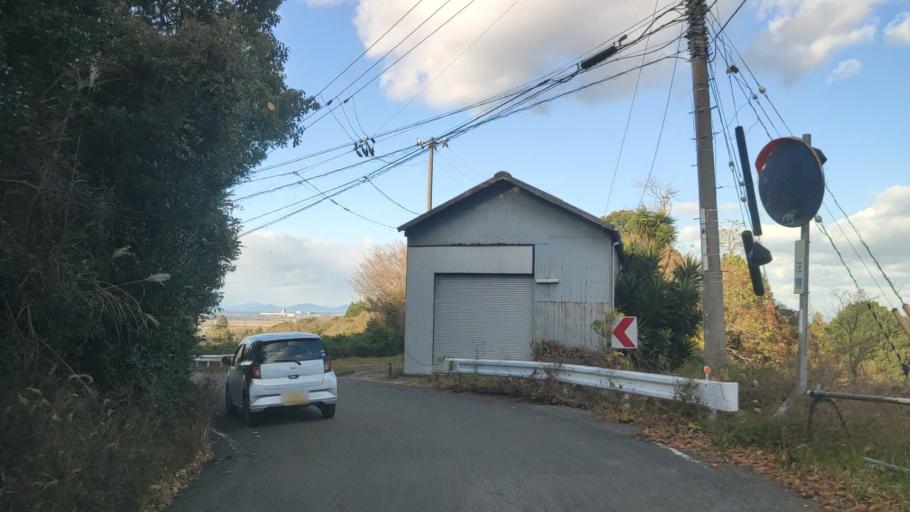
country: JP
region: Ehime
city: Saijo
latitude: 33.8852
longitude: 133.1306
